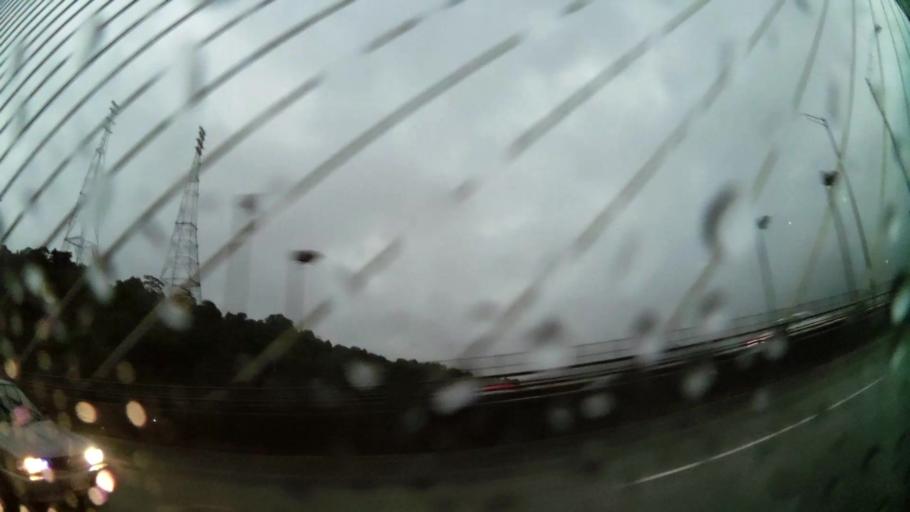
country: PA
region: Panama
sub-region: Distrito de Panama
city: Paraiso
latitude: 9.0332
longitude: -79.6333
